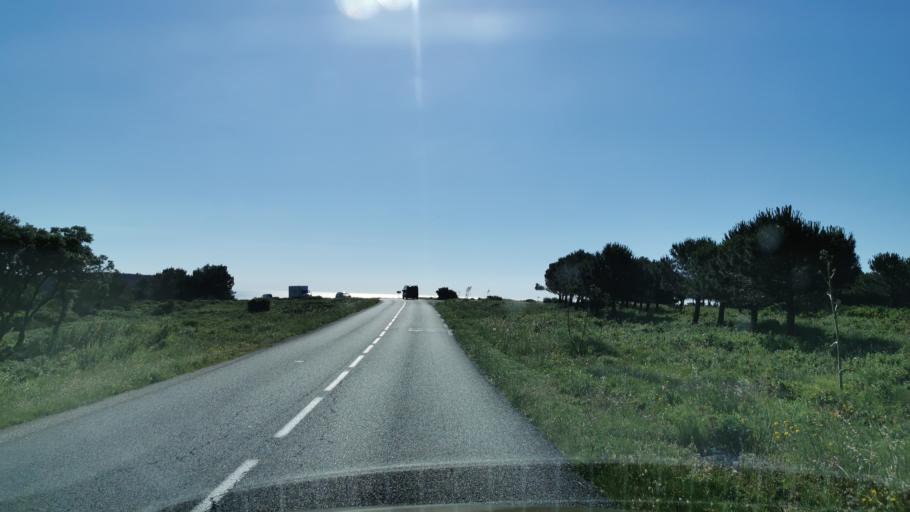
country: FR
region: Languedoc-Roussillon
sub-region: Departement de l'Aude
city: Armissan
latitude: 43.1694
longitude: 3.1282
